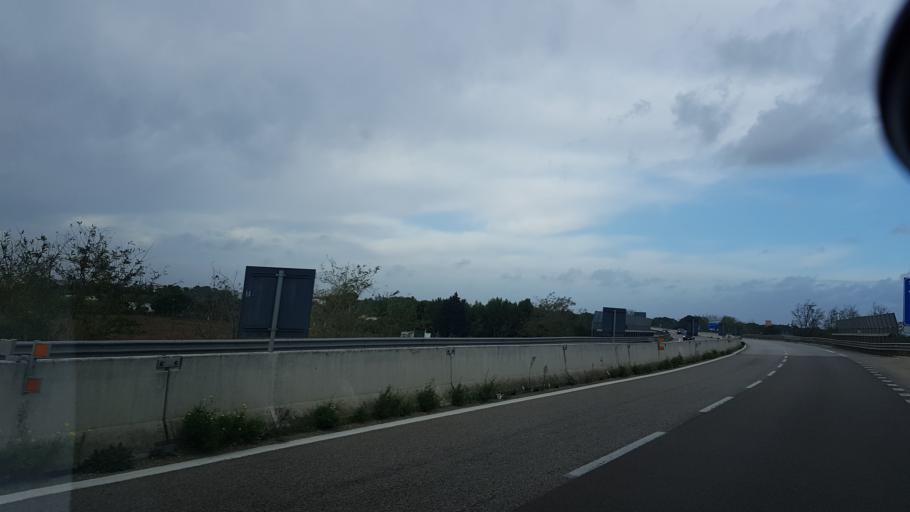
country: IT
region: Apulia
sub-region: Provincia di Brindisi
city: Mesagne
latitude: 40.5711
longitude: 17.8114
